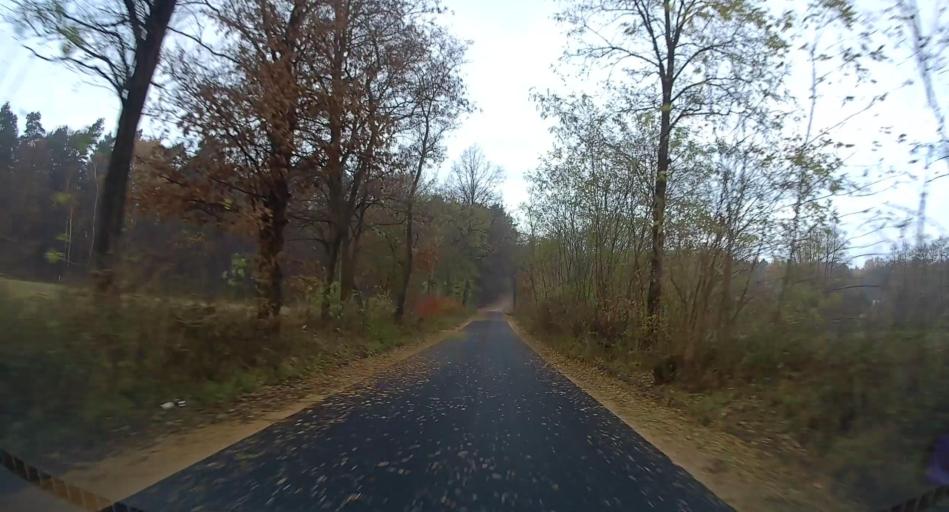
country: PL
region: Lodz Voivodeship
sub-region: Powiat skierniewicki
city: Kowiesy
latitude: 51.9298
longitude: 20.3985
